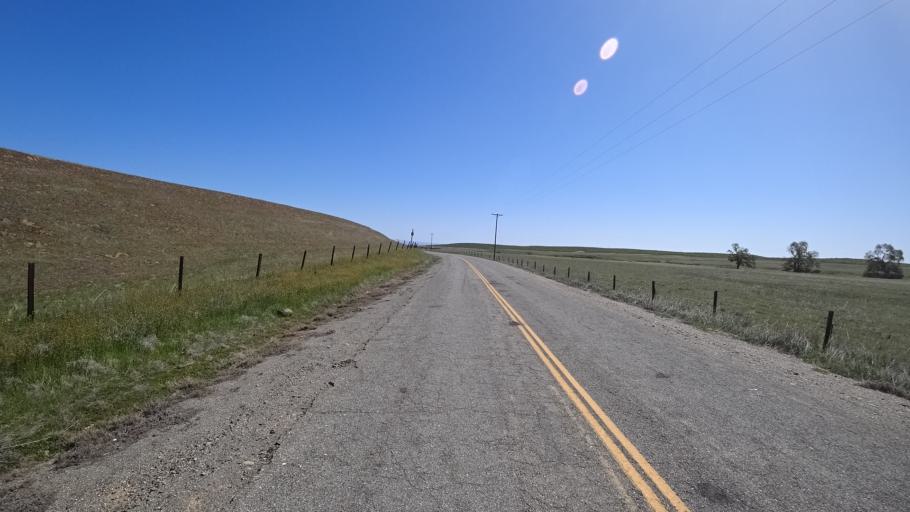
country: US
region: California
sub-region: Glenn County
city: Orland
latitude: 39.7802
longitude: -122.3035
